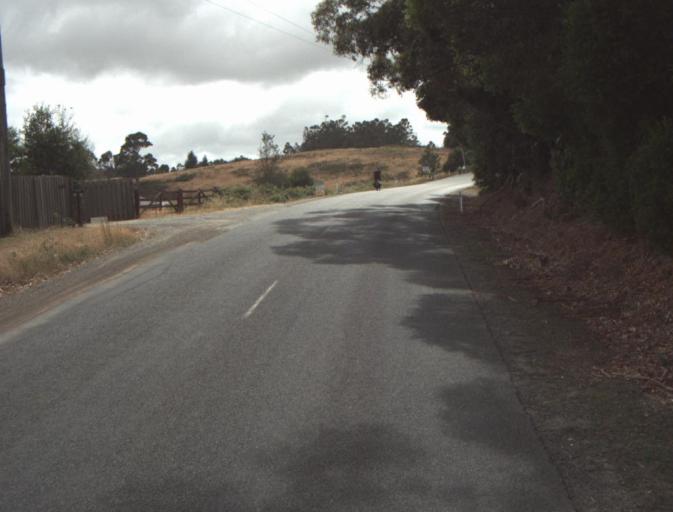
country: AU
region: Tasmania
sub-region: Launceston
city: Mayfield
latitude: -41.2108
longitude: 147.2132
